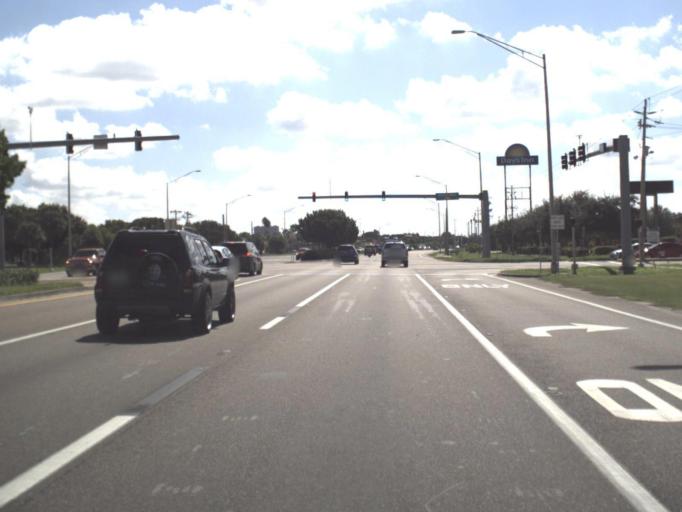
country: US
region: Florida
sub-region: Lee County
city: North Fort Myers
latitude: 26.6644
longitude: -81.8874
